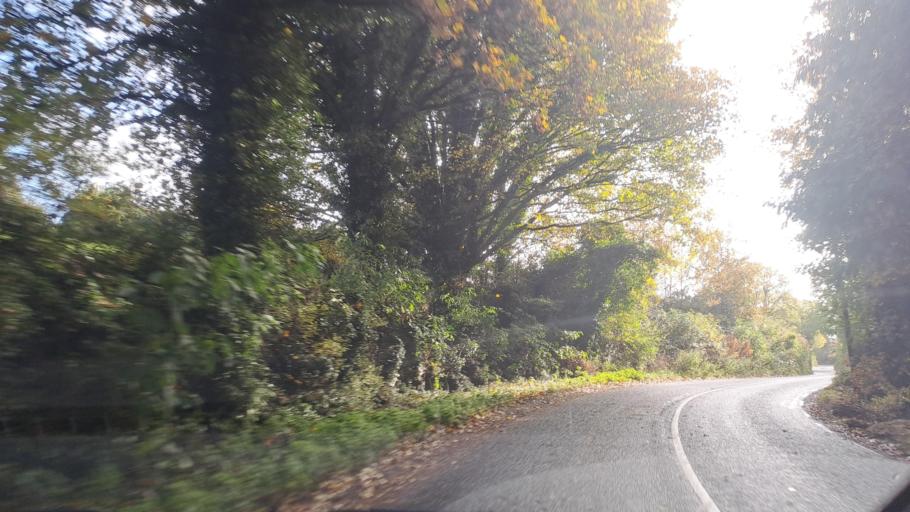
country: IE
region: Ulster
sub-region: County Monaghan
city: Carrickmacross
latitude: 53.9278
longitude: -6.7162
